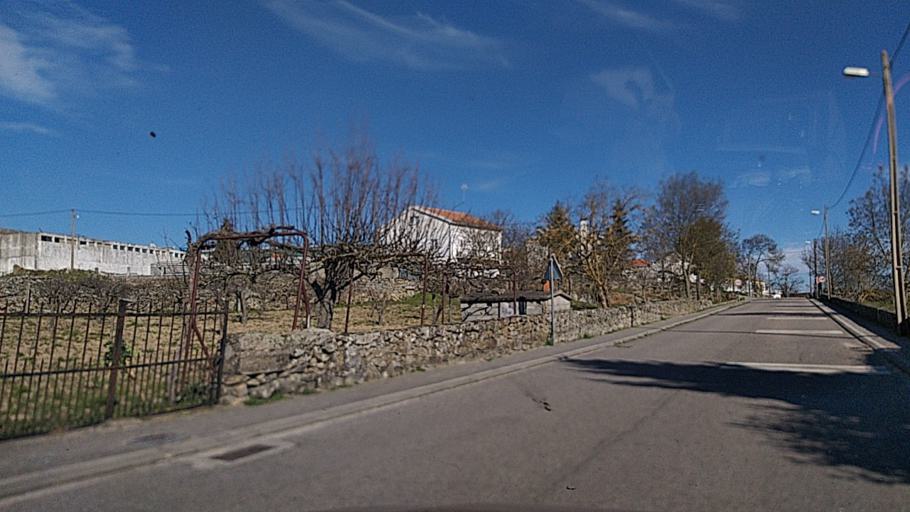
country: PT
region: Guarda
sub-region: Guarda
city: Sequeira
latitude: 40.6017
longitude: -7.0630
